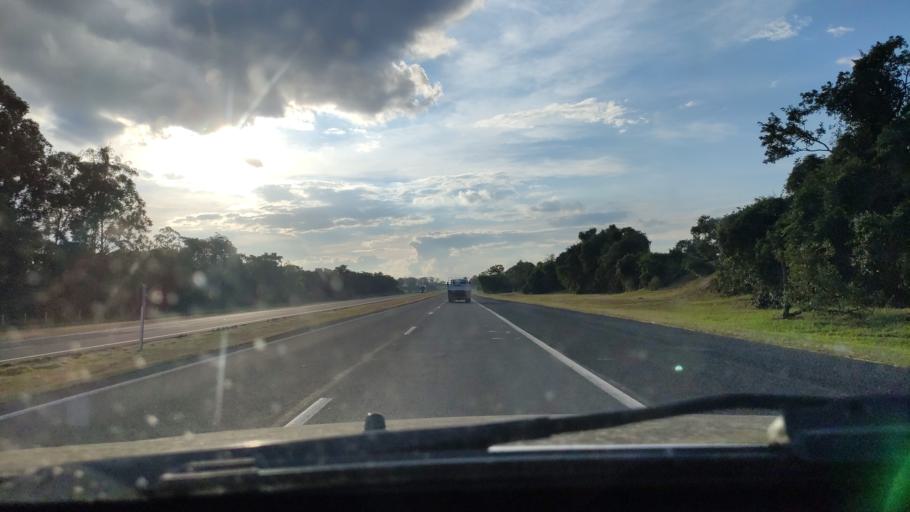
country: BR
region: Sao Paulo
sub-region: Rancharia
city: Rancharia
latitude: -22.4667
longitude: -50.9543
